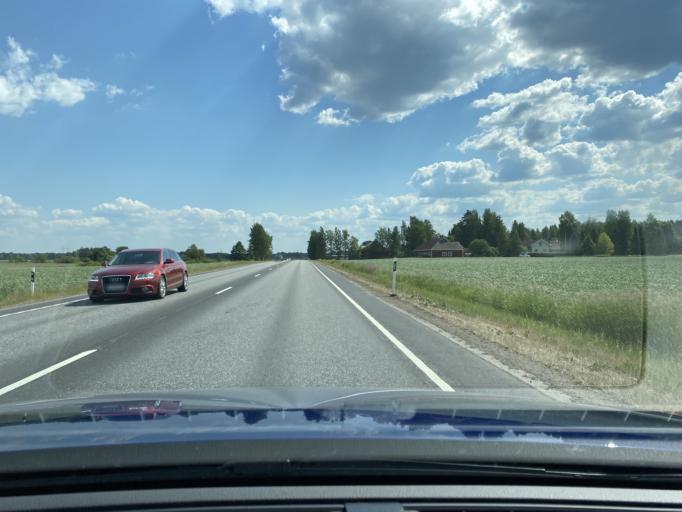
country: FI
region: Satakunta
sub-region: Rauma
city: Eura
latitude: 61.1515
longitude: 22.0979
